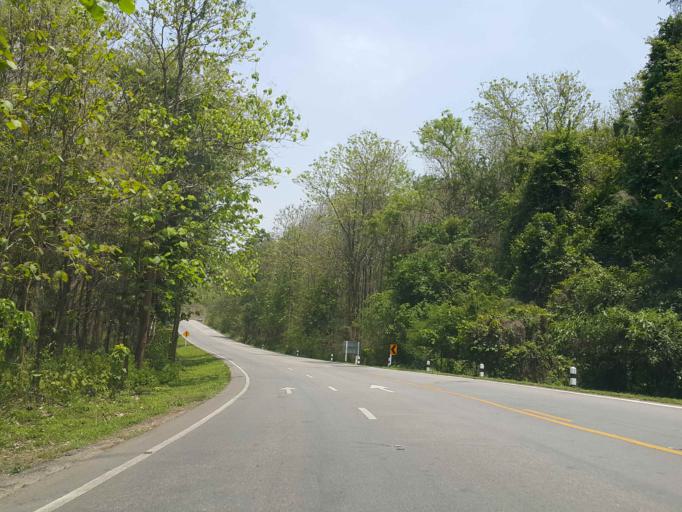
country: TH
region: Chiang Mai
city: Mae On
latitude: 18.9373
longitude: 99.2381
